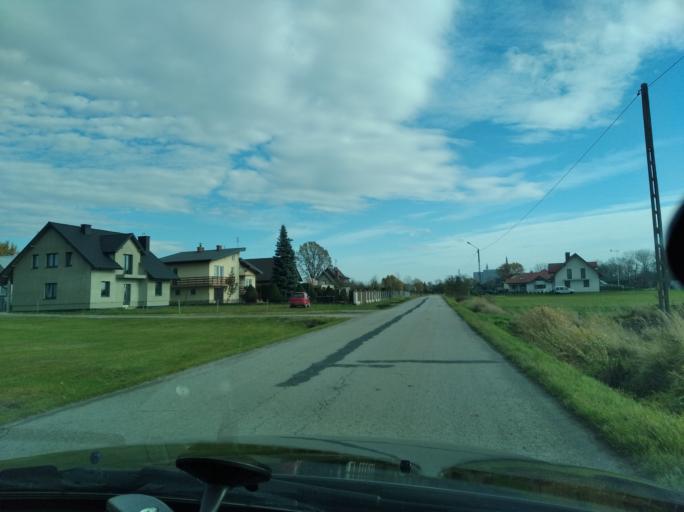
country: PL
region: Subcarpathian Voivodeship
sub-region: Powiat ropczycko-sedziszowski
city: Ostrow
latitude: 50.0968
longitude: 21.5467
